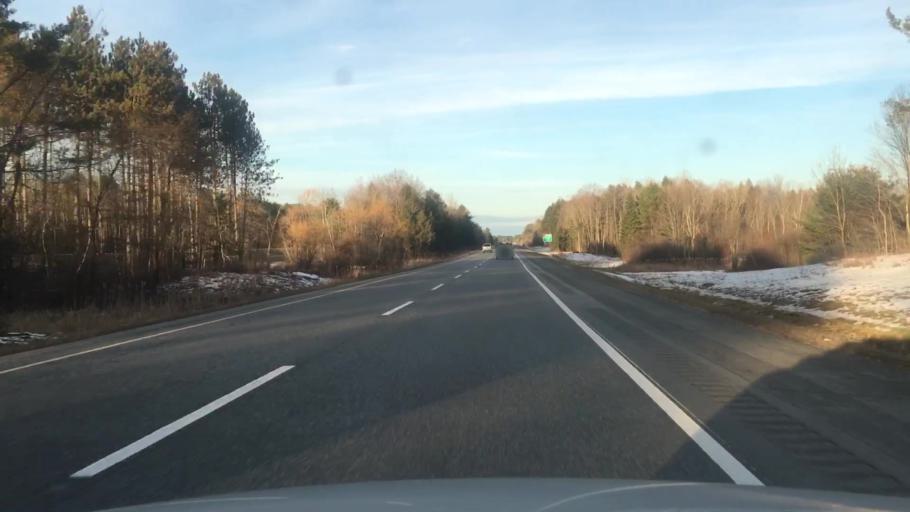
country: US
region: Maine
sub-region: Kennebec County
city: Sidney
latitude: 44.4368
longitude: -69.7289
